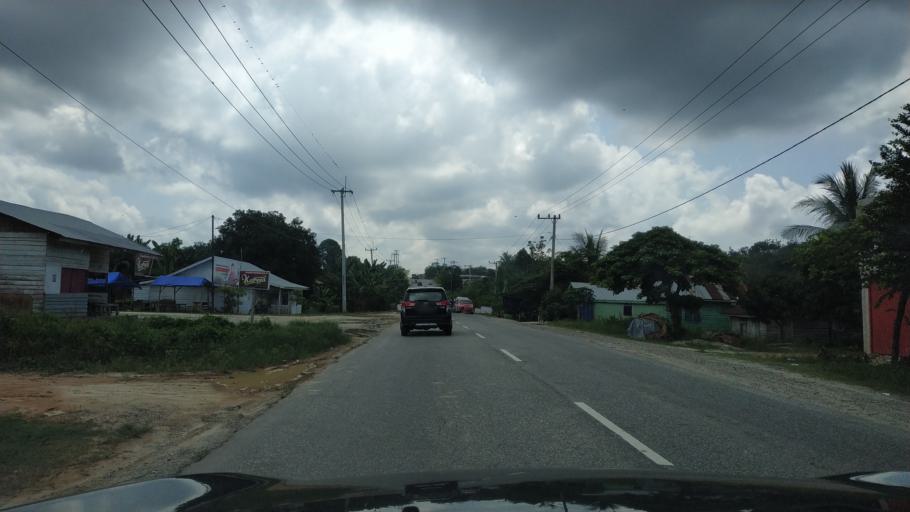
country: ID
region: Riau
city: Pangkalanbunut
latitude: 0.3038
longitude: 101.9117
